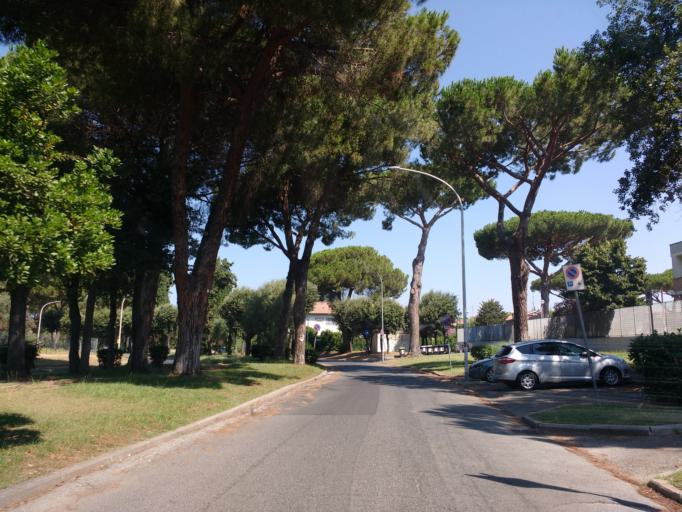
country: IT
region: Latium
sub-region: Citta metropolitana di Roma Capitale
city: Acilia-Castel Fusano-Ostia Antica
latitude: 41.7577
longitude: 12.3604
